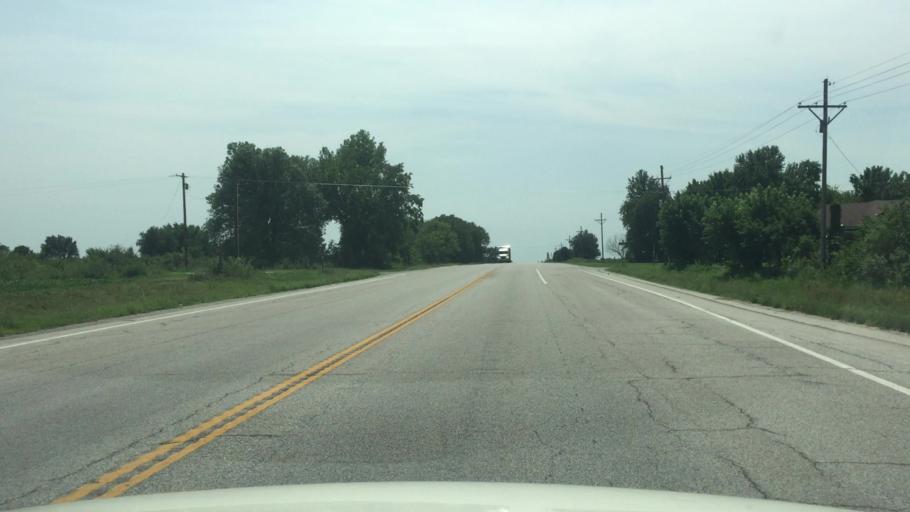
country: US
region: Kansas
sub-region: Cherokee County
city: Galena
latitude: 37.1052
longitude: -94.7044
